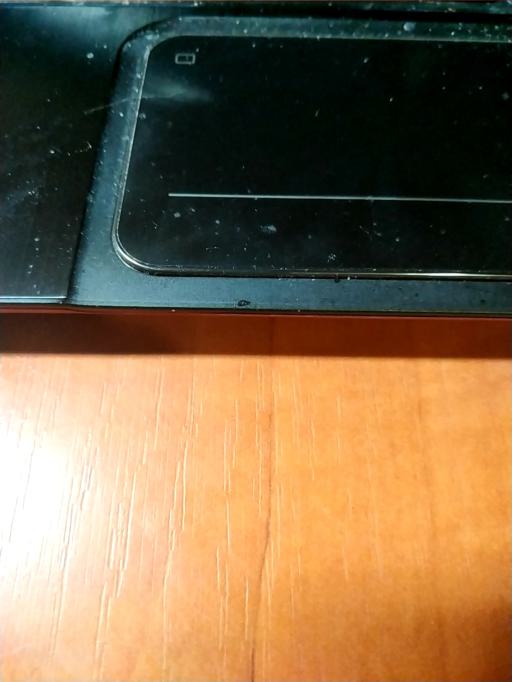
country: RU
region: Tverskaya
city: Ves'yegonsk
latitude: 58.7304
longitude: 37.5438
